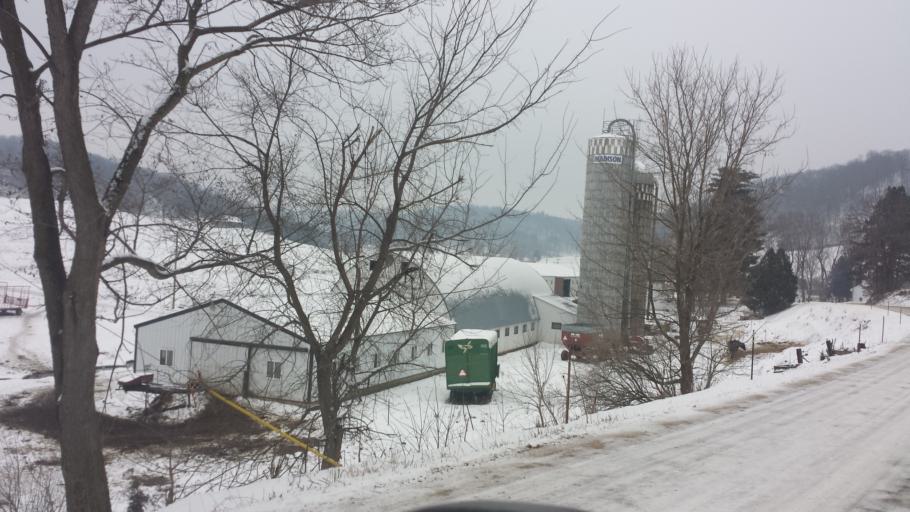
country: US
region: Wisconsin
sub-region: Monroe County
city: Cashton
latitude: 43.7246
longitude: -90.6666
